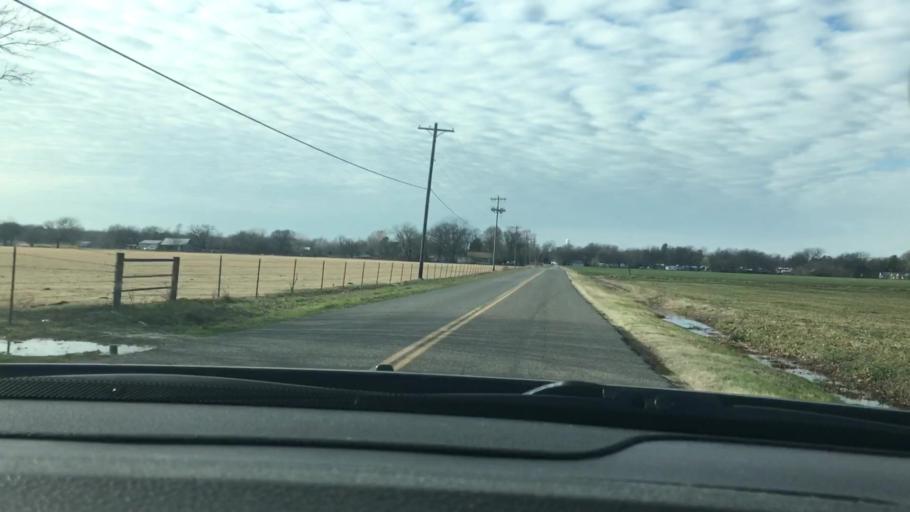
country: US
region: Oklahoma
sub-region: Garvin County
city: Pauls Valley
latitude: 34.7388
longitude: -97.2005
